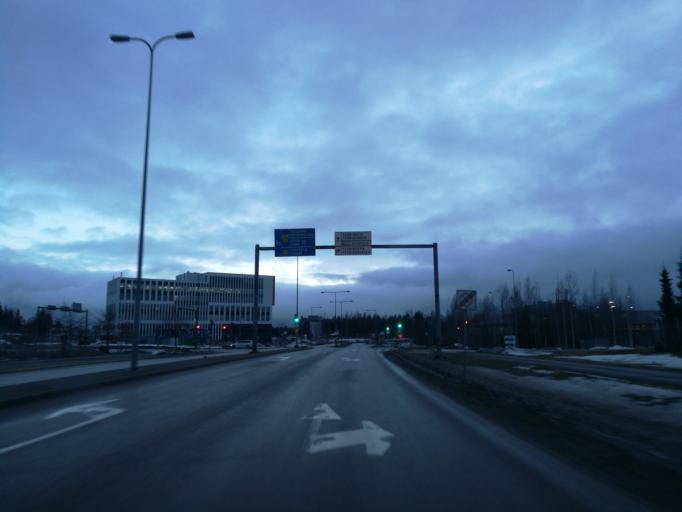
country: FI
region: Uusimaa
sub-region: Helsinki
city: Vantaa
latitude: 60.3090
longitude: 24.9622
